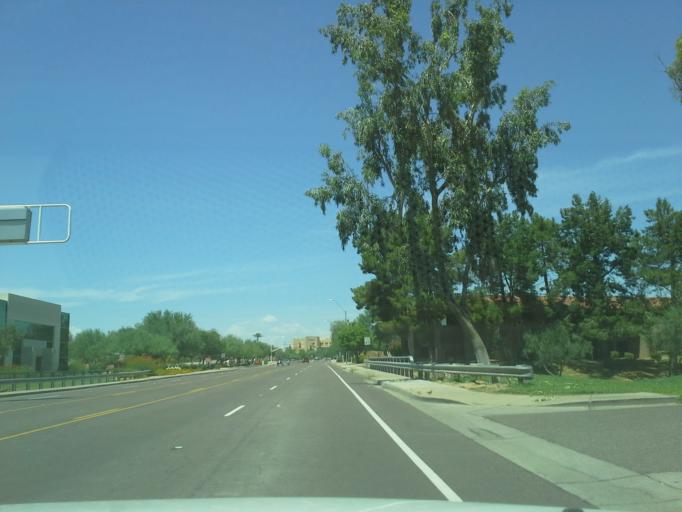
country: US
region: Arizona
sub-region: Maricopa County
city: Scottsdale
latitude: 33.5725
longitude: -111.8866
